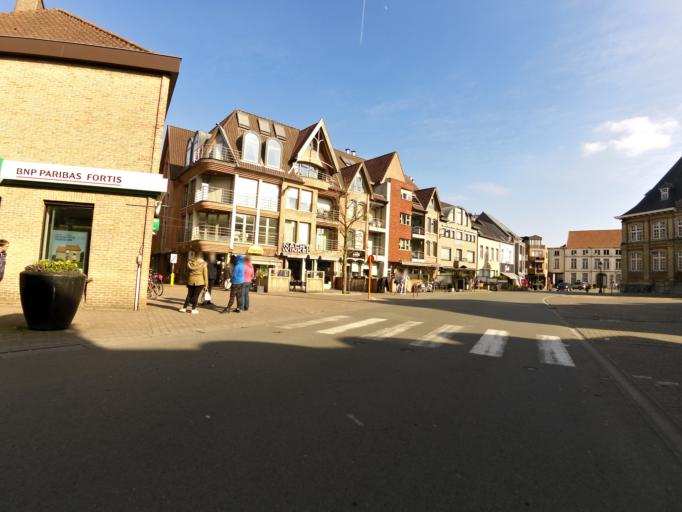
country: BE
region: Flanders
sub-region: Provincie West-Vlaanderen
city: Torhout
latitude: 51.0651
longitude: 3.1013
